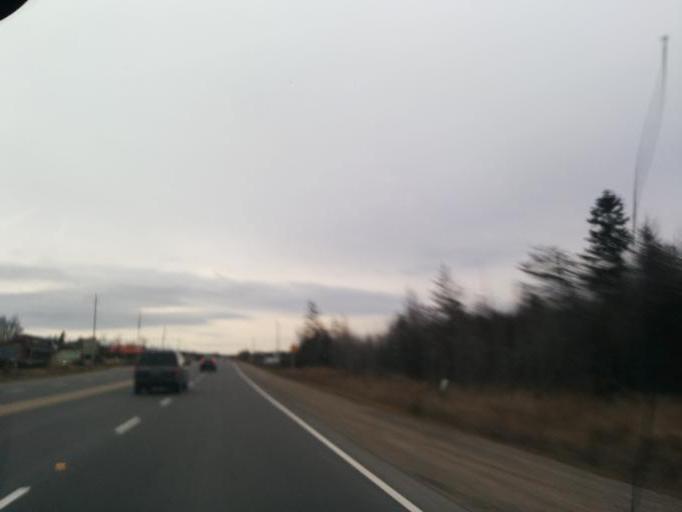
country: CA
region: Ontario
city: Shelburne
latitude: 44.0900
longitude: -80.1449
